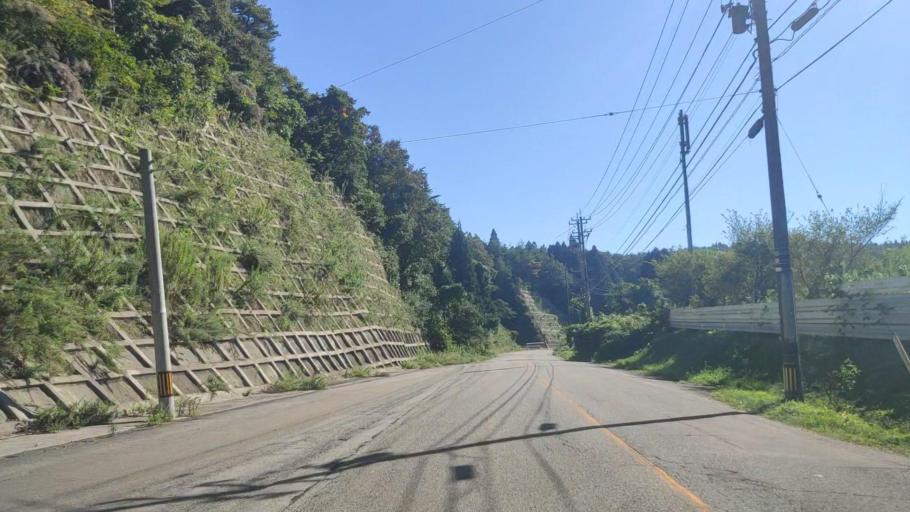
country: JP
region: Ishikawa
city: Nanao
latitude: 37.3177
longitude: 137.1650
